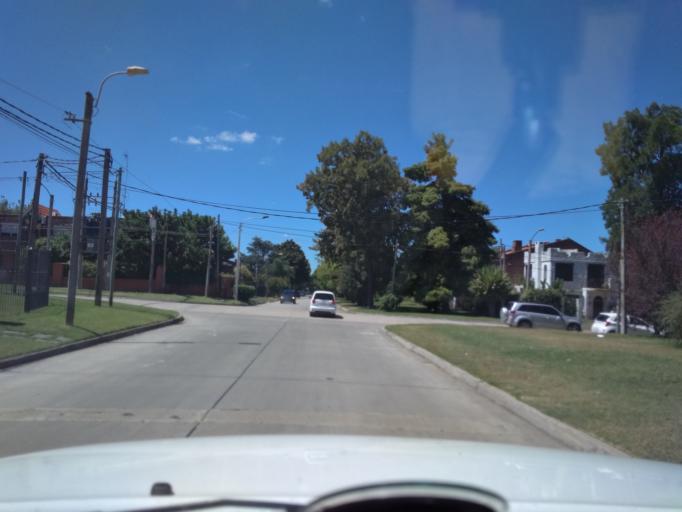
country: UY
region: Canelones
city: Paso de Carrasco
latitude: -34.8814
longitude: -56.0752
